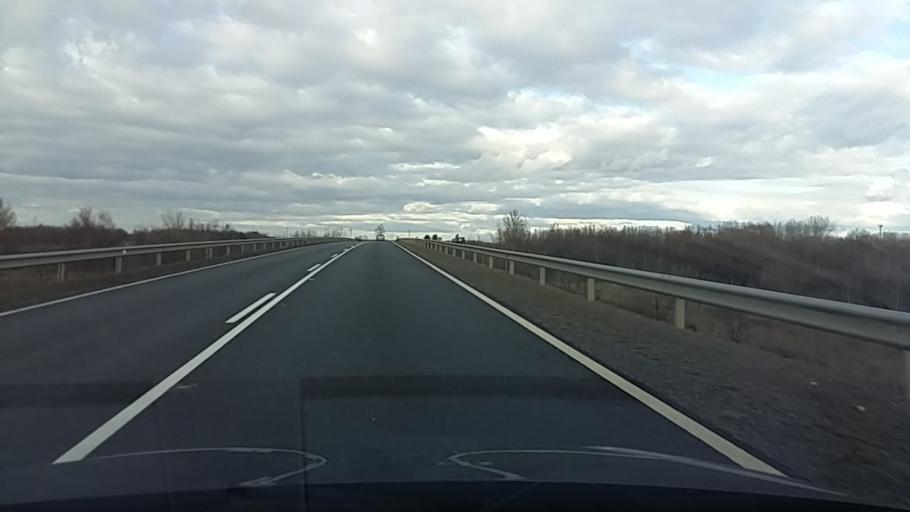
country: HU
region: Szabolcs-Szatmar-Bereg
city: Nyirpazony
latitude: 47.9448
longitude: 21.8192
